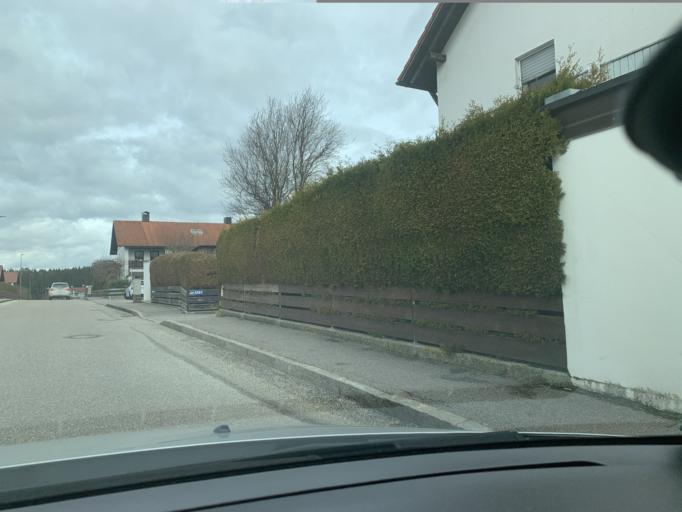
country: DE
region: Bavaria
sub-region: Lower Bavaria
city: Vilsbiburg
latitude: 48.4596
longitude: 12.3524
